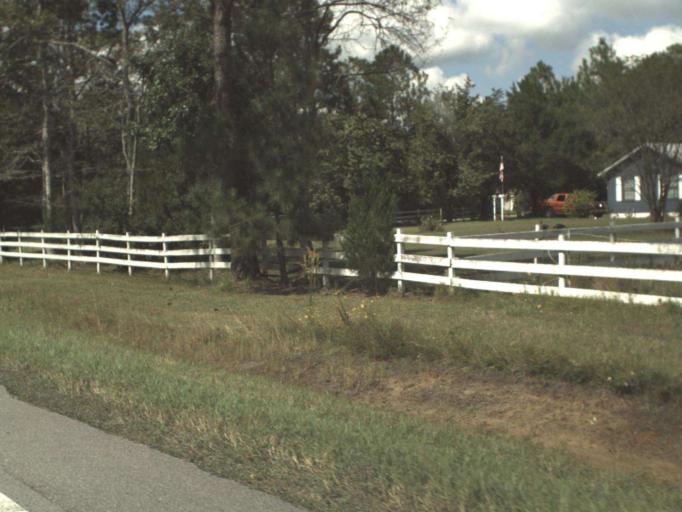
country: US
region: Florida
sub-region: Walton County
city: Freeport
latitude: 30.4780
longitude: -86.0551
